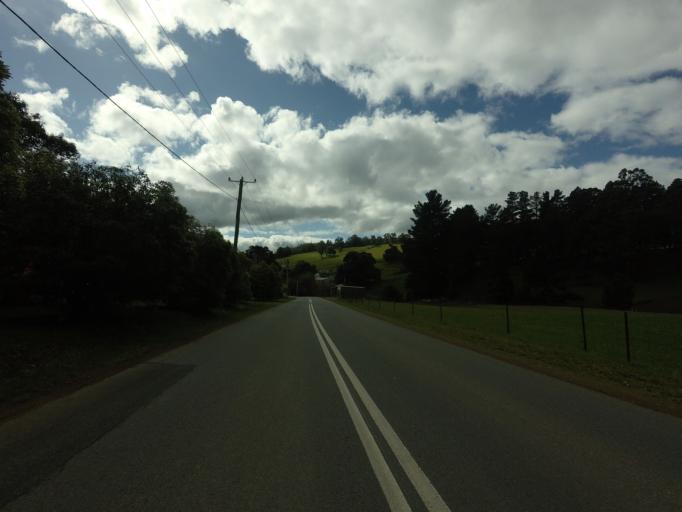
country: AU
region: Tasmania
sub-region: Huon Valley
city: Geeveston
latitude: -43.2411
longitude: 146.9919
